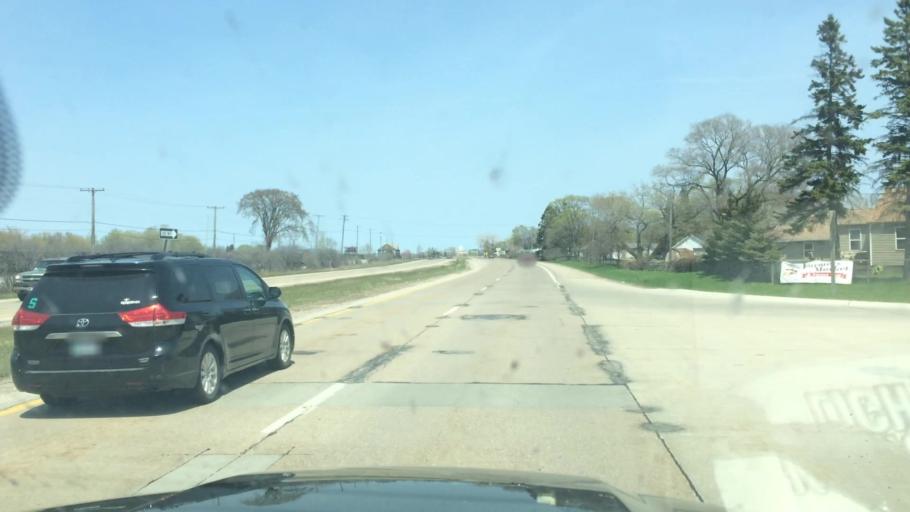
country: US
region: Michigan
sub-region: Delta County
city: Gladstone
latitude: 45.8418
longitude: -87.0339
